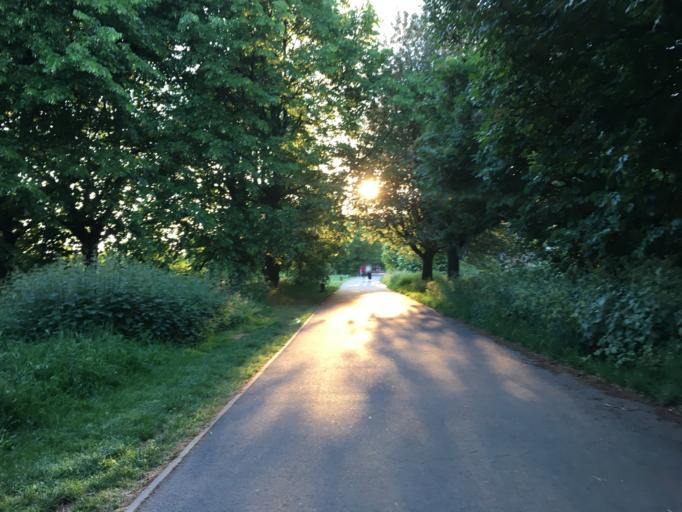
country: GB
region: England
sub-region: Greater London
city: Camden Town
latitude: 51.5337
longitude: -0.1542
